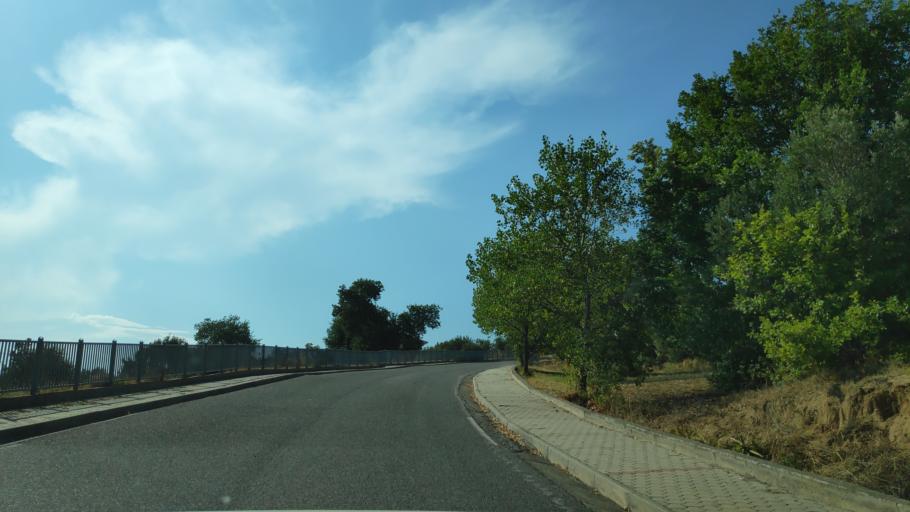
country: IT
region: Calabria
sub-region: Provincia di Catanzaro
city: Soverato Superiore
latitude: 38.6857
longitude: 16.5375
